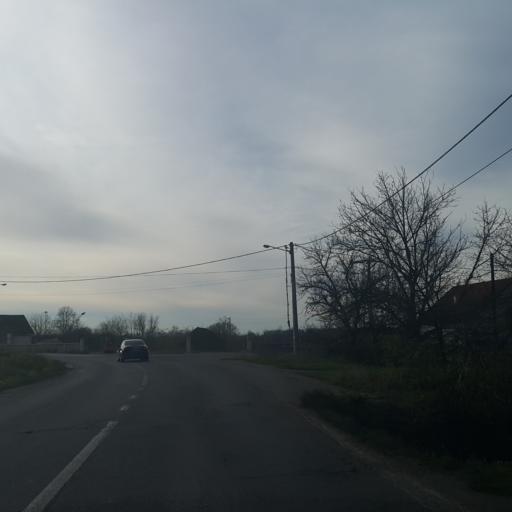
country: RS
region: Central Serbia
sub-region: Belgrade
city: Lazarevac
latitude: 44.4049
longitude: 20.2608
